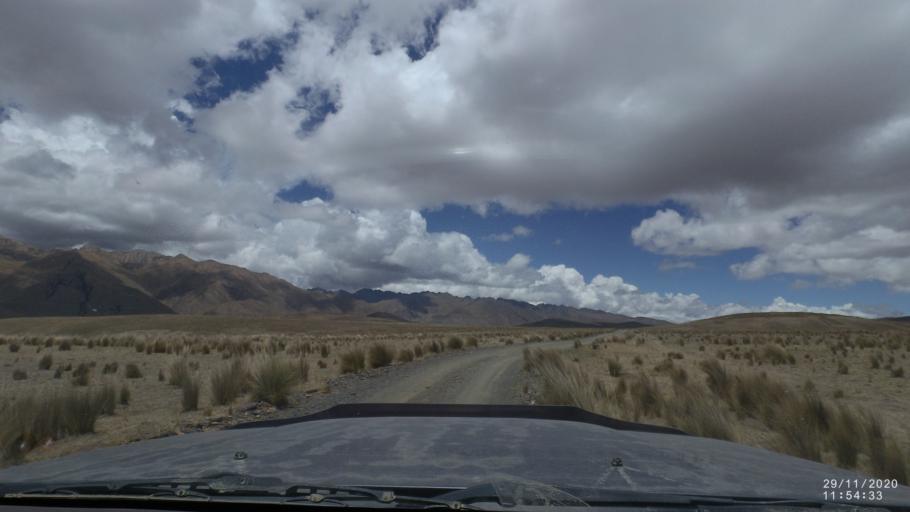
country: BO
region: Cochabamba
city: Cochabamba
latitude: -17.1642
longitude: -66.2705
